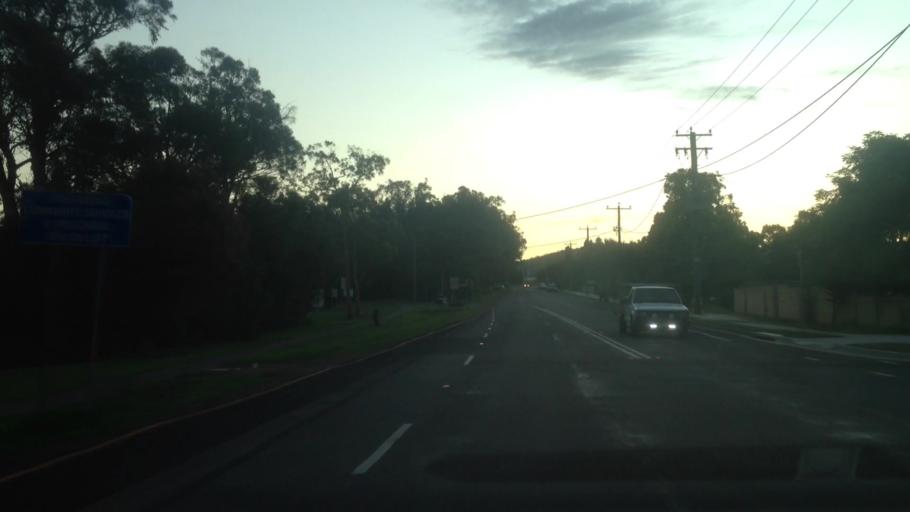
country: AU
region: New South Wales
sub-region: Lake Macquarie Shire
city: Cooranbong
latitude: -33.0737
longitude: 151.4583
